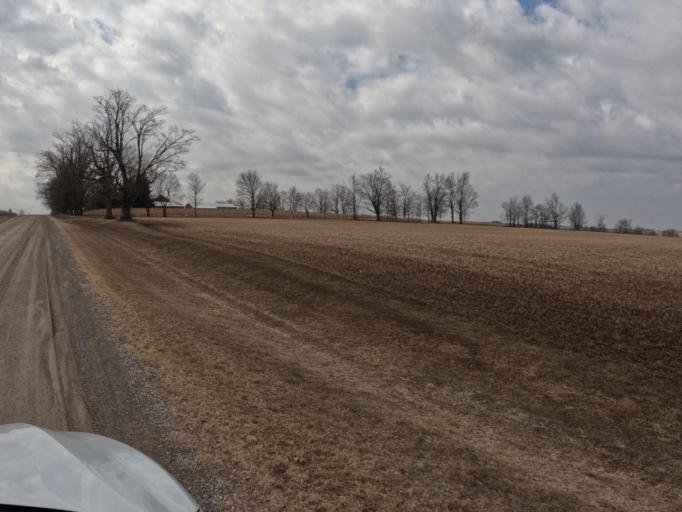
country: CA
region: Ontario
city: Shelburne
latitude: 43.9408
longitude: -80.2439
